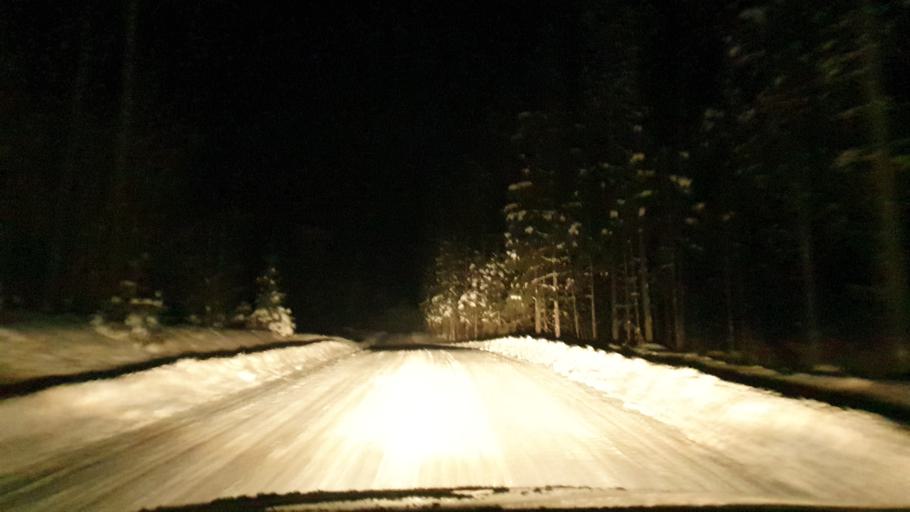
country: EE
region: Vorumaa
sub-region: Antsla vald
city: Vana-Antsla
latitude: 57.9462
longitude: 26.6143
